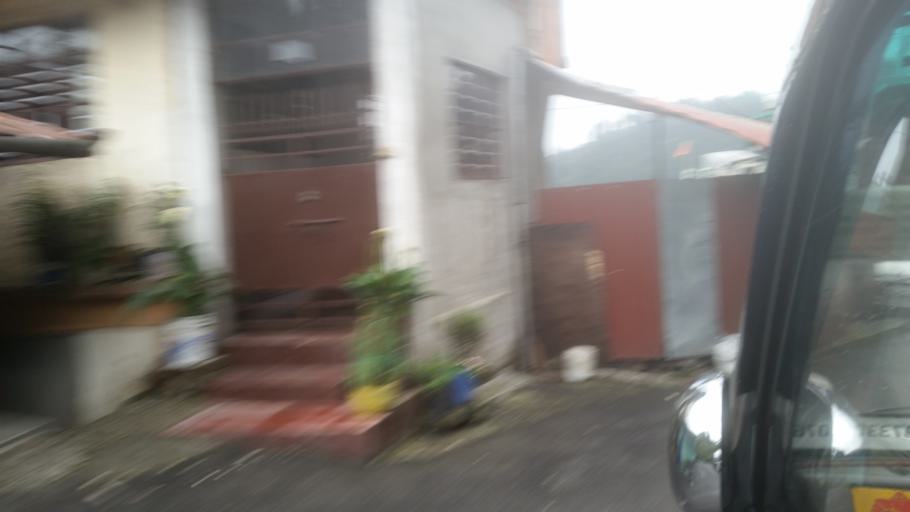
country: IN
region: West Bengal
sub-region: Darjiling
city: Darjiling
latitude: 27.0050
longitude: 88.2618
